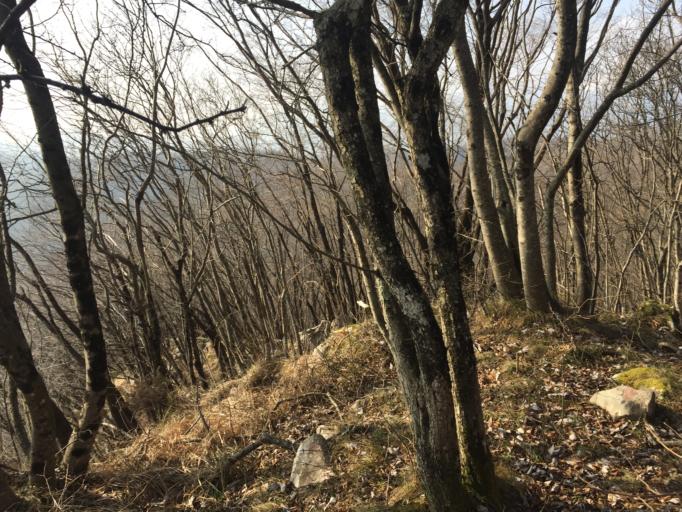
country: IT
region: Friuli Venezia Giulia
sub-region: Provincia di Udine
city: Taipana
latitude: 46.2547
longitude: 13.3064
